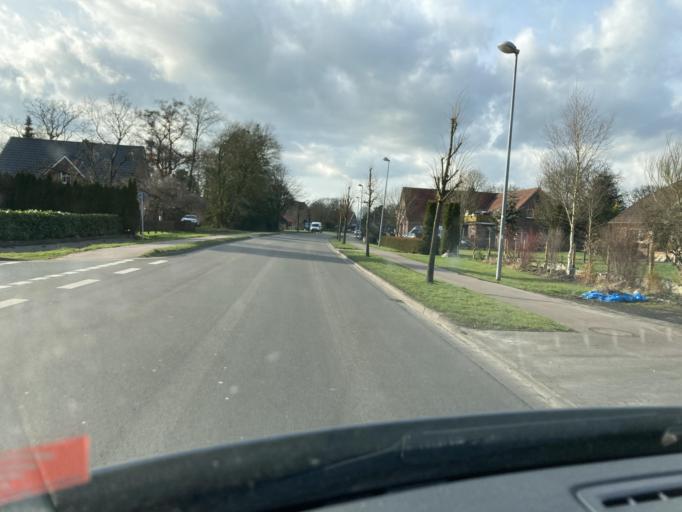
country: DE
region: Lower Saxony
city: Nortmoor
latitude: 53.1593
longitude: 7.5263
